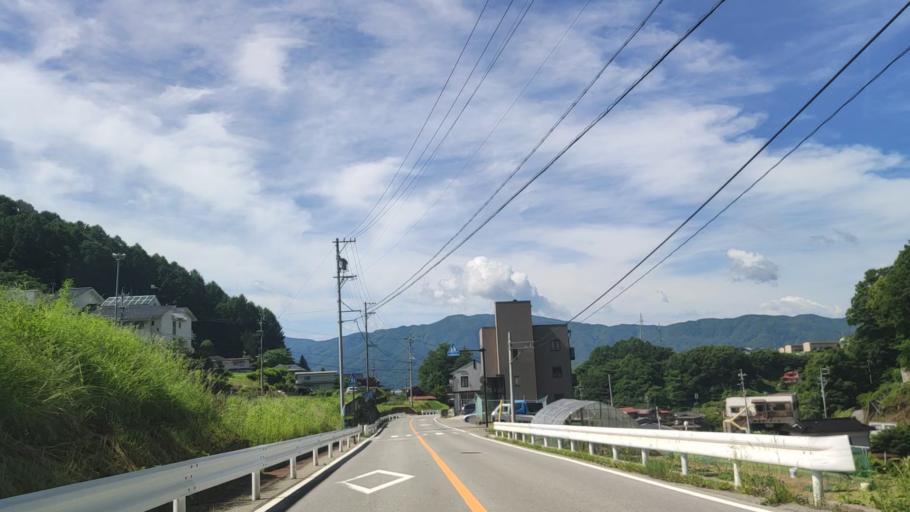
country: JP
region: Nagano
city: Suwa
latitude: 36.0523
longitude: 138.1283
